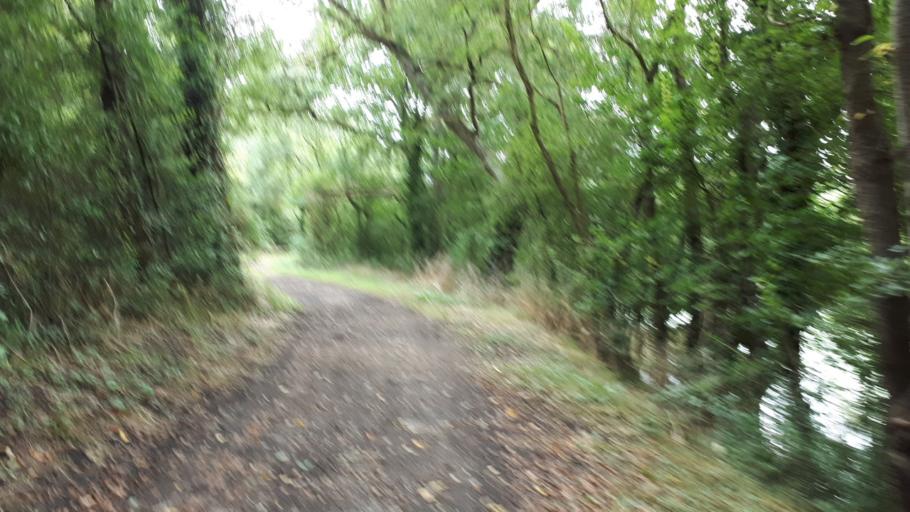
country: FR
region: Pays de la Loire
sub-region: Departement de Maine-et-Loire
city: Rochefort-sur-Loire
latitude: 47.3344
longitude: -0.6908
